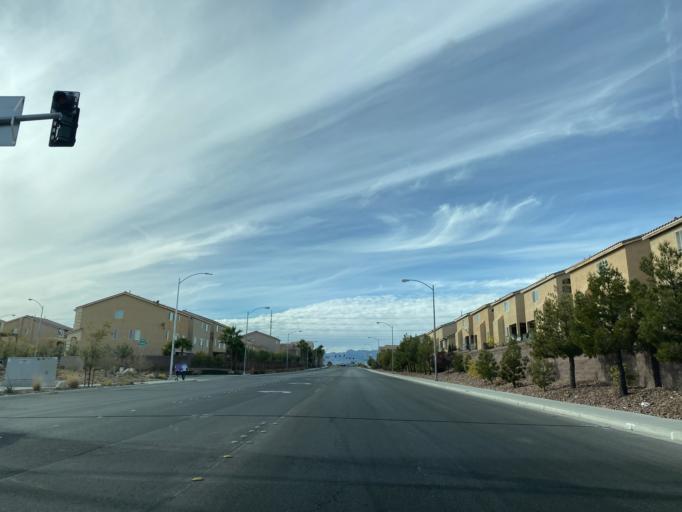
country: US
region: Nevada
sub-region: Clark County
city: Enterprise
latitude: 36.0342
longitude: -115.2393
